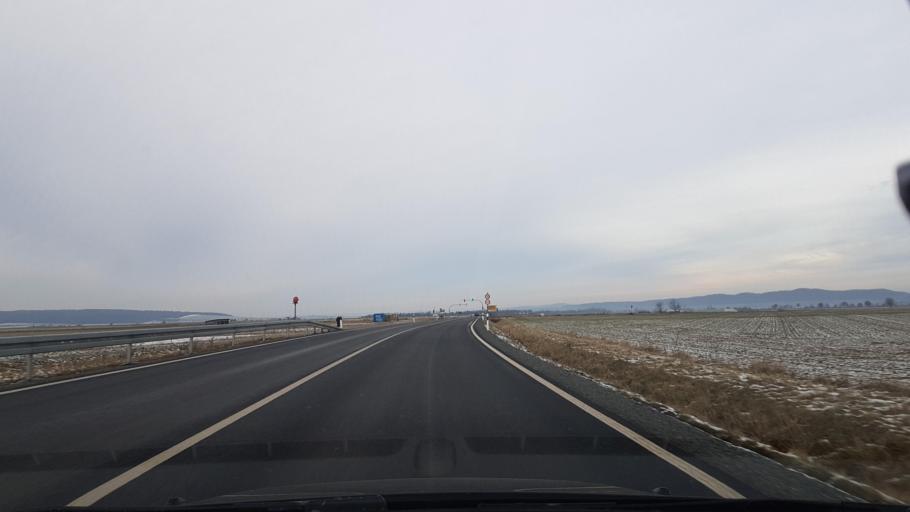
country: DE
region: Lower Saxony
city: Langelsheim
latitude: 51.9576
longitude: 10.3825
